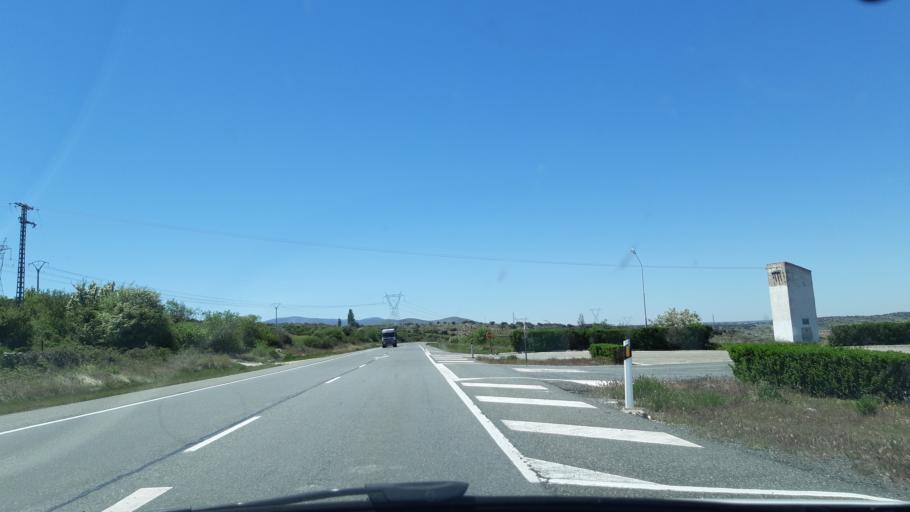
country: ES
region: Castille and Leon
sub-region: Provincia de Segovia
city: Vegas de Matute
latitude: 40.7491
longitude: -4.2974
